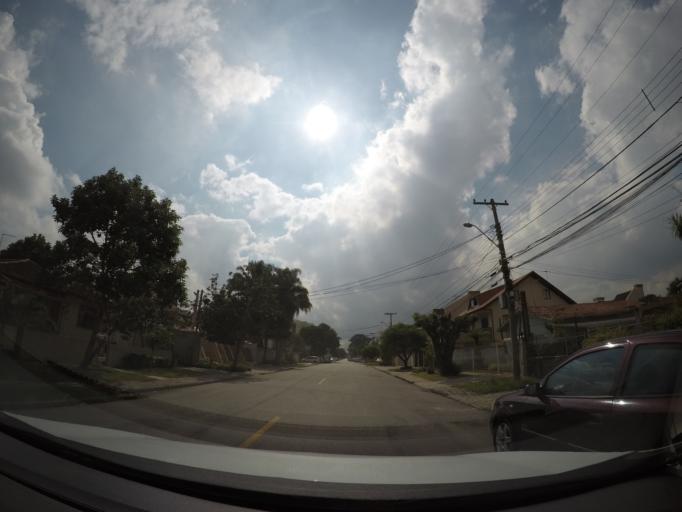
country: BR
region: Parana
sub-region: Curitiba
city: Curitiba
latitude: -25.4836
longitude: -49.2503
